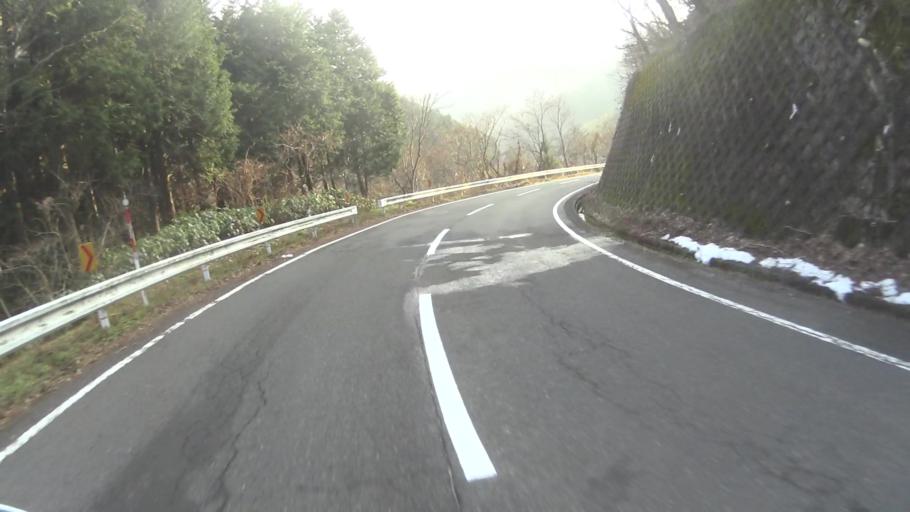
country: JP
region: Kyoto
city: Maizuru
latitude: 35.4156
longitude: 135.4112
